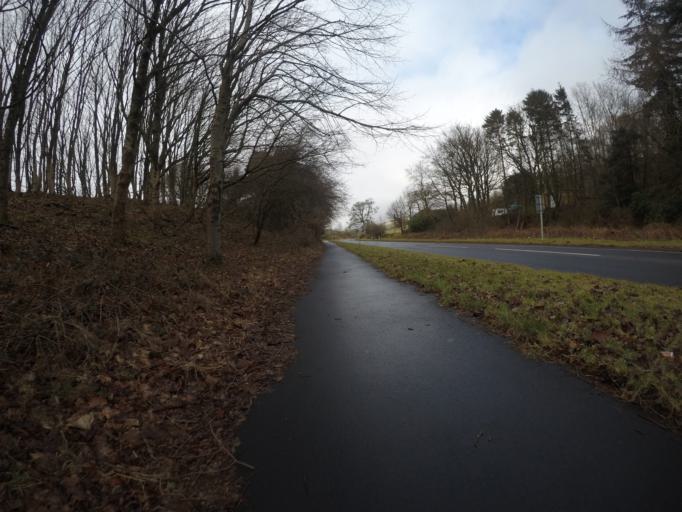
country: GB
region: Scotland
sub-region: North Ayrshire
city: Fairlie
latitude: 55.7306
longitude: -4.8647
